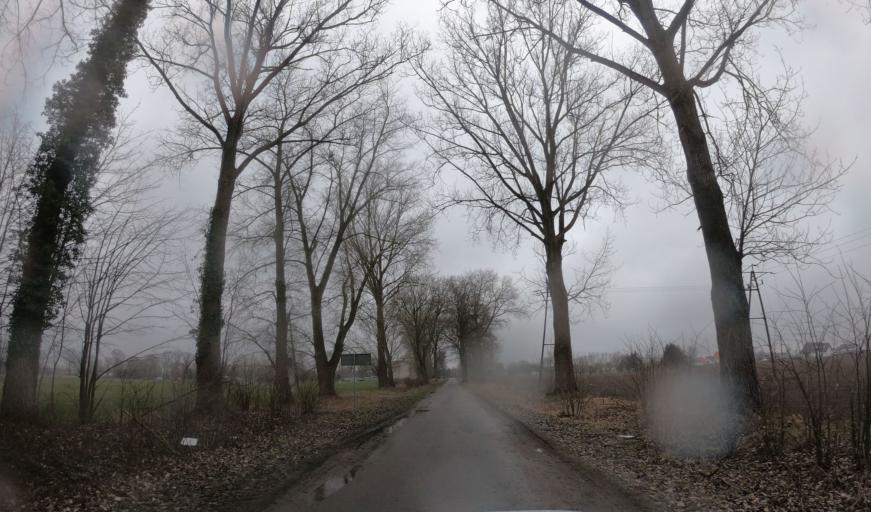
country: PL
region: West Pomeranian Voivodeship
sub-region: Powiat kamienski
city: Kamien Pomorski
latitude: 53.9040
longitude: 14.8304
